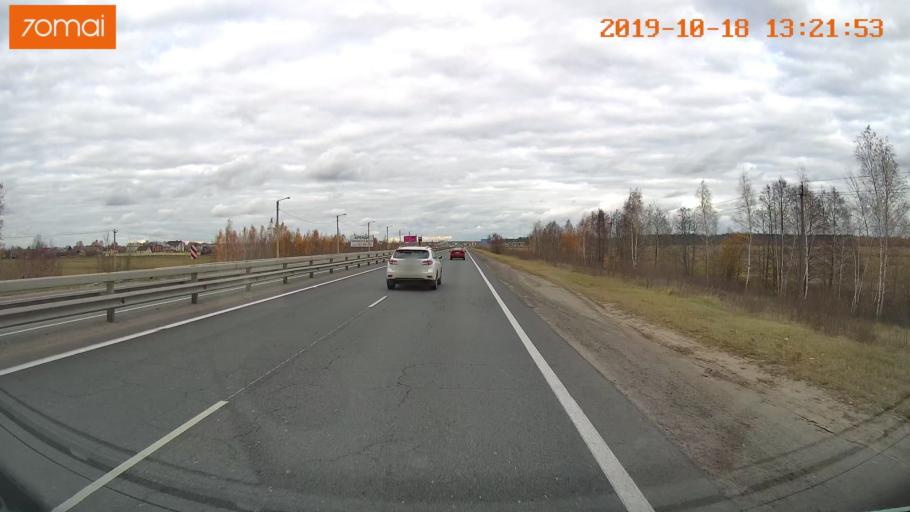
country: RU
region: Rjazan
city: Polyany
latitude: 54.7015
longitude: 39.8426
